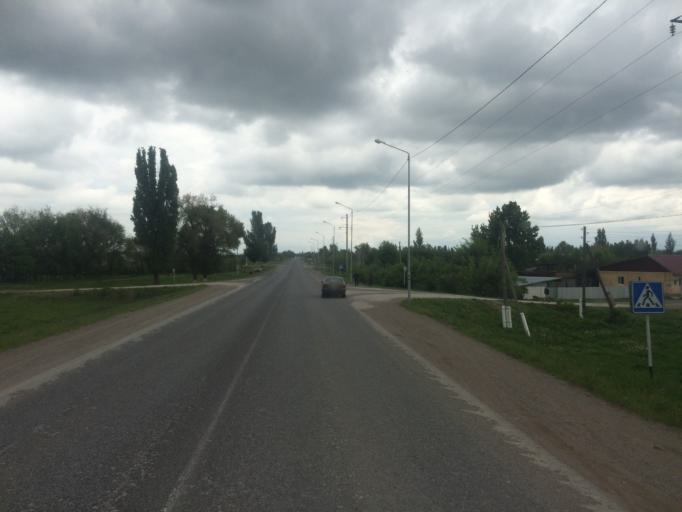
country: KZ
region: Zhambyl
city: Georgiyevka
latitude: 43.1394
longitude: 74.6206
